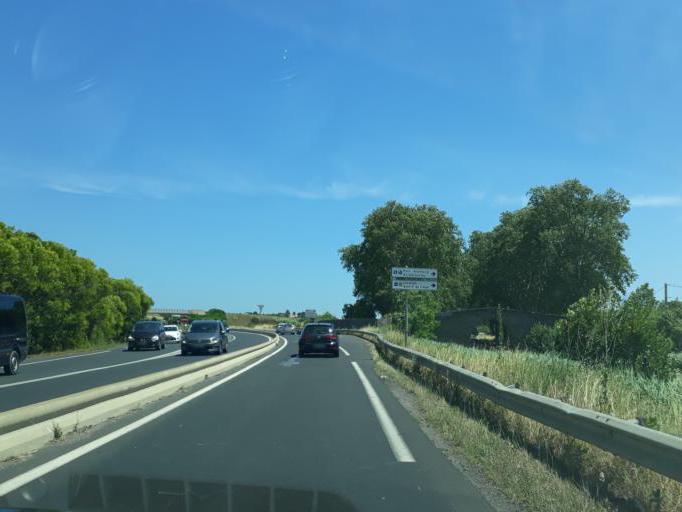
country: FR
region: Languedoc-Roussillon
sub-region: Departement de l'Herault
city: Cers
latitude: 43.3153
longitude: 3.3121
